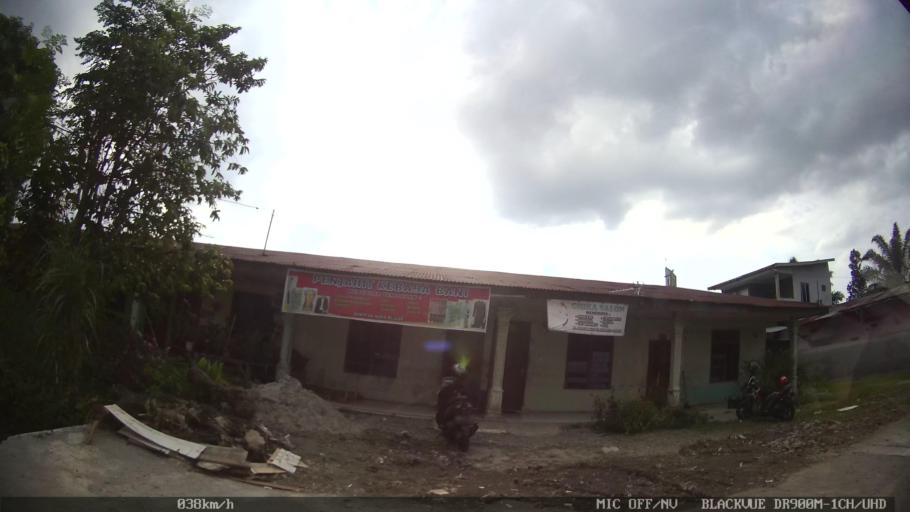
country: ID
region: North Sumatra
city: Sunggal
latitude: 3.5392
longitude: 98.6053
